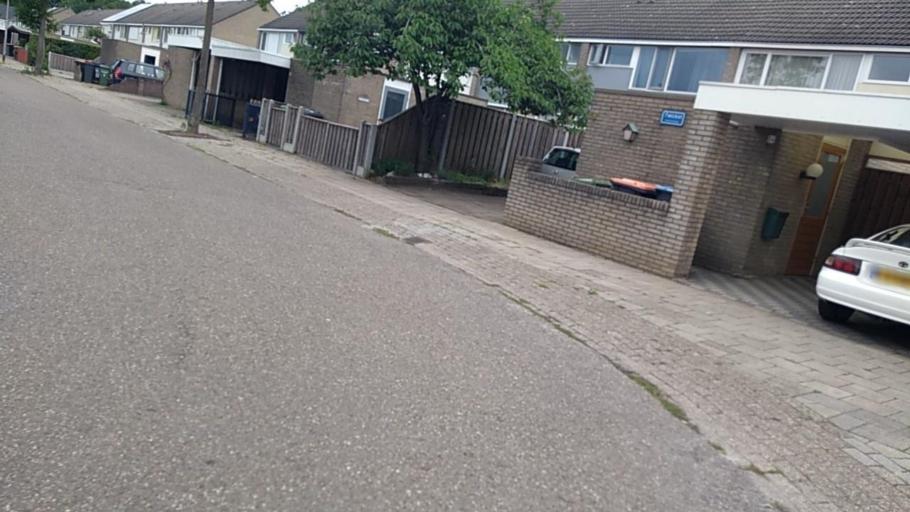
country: NL
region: Overijssel
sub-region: Gemeente Almelo
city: Almelo
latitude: 52.3797
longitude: 6.6827
